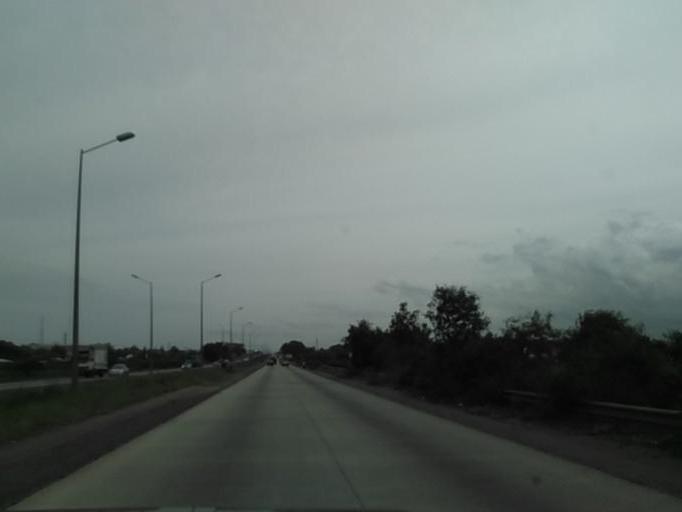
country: GH
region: Greater Accra
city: Medina Estates
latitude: 5.6449
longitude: -0.1188
